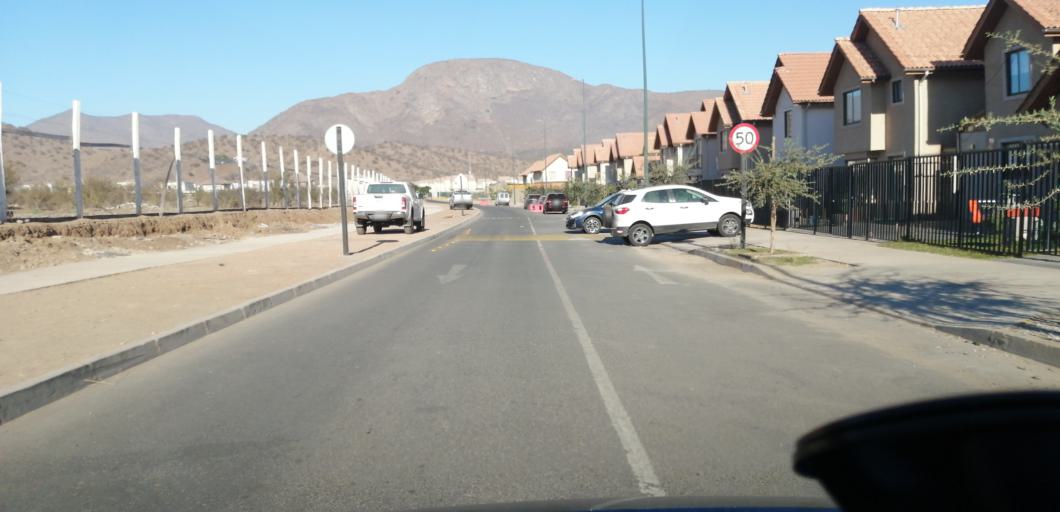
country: CL
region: Santiago Metropolitan
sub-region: Provincia de Santiago
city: Lo Prado
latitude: -33.4658
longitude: -70.8581
